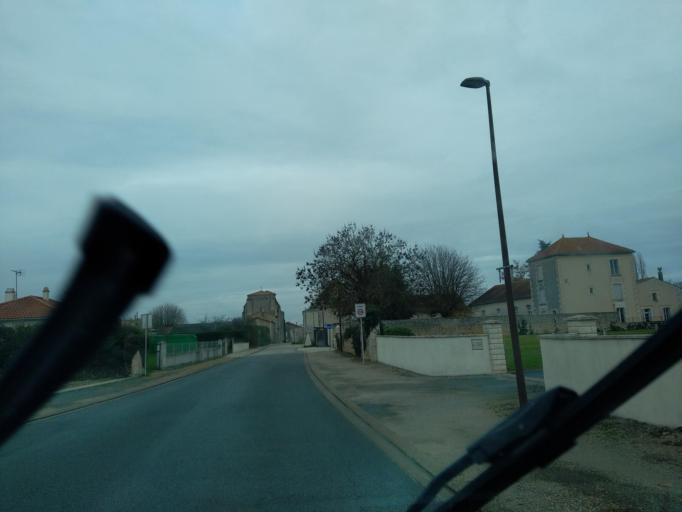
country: FR
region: Pays de la Loire
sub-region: Departement de la Vendee
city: Maillezais
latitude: 46.3708
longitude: -0.7362
